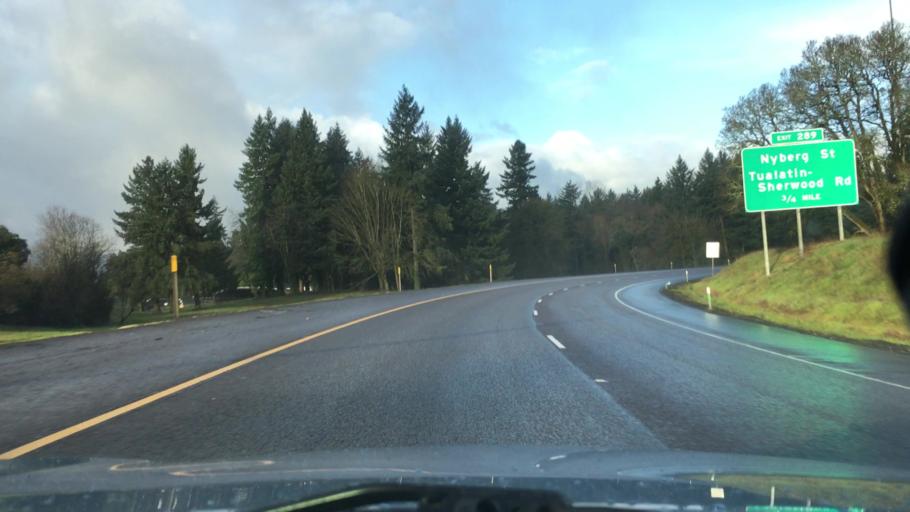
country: US
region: Oregon
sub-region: Washington County
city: Tualatin
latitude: 45.3703
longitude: -122.7521
